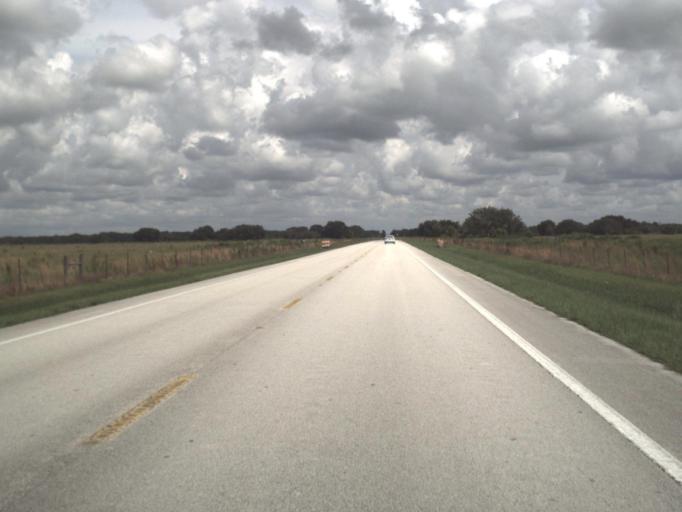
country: US
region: Florida
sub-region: Sarasota County
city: Warm Mineral Springs
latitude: 27.1935
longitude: -82.1731
